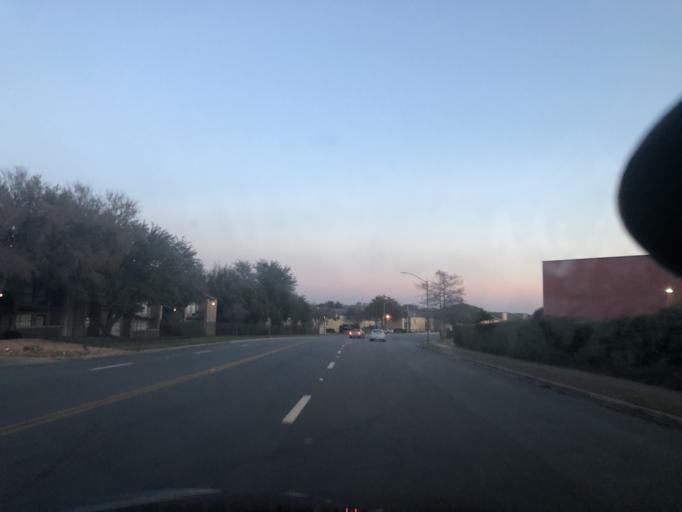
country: US
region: Texas
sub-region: Tarrant County
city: White Settlement
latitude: 32.7267
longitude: -97.4775
